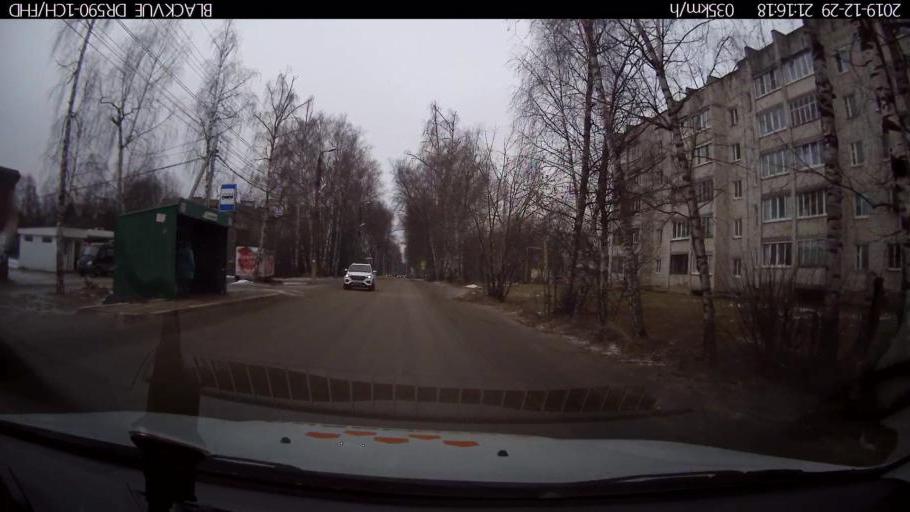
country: RU
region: Nizjnij Novgorod
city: Afonino
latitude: 56.2105
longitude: 44.0229
